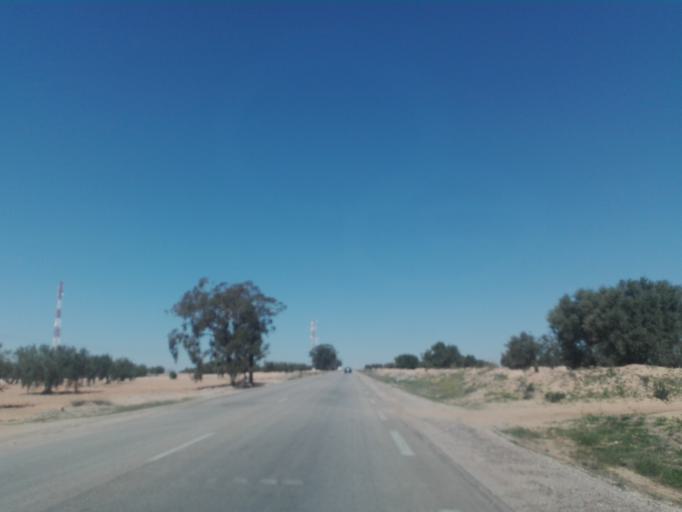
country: TN
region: Safaqis
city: Bi'r `Ali Bin Khalifah
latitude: 34.7546
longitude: 10.3341
